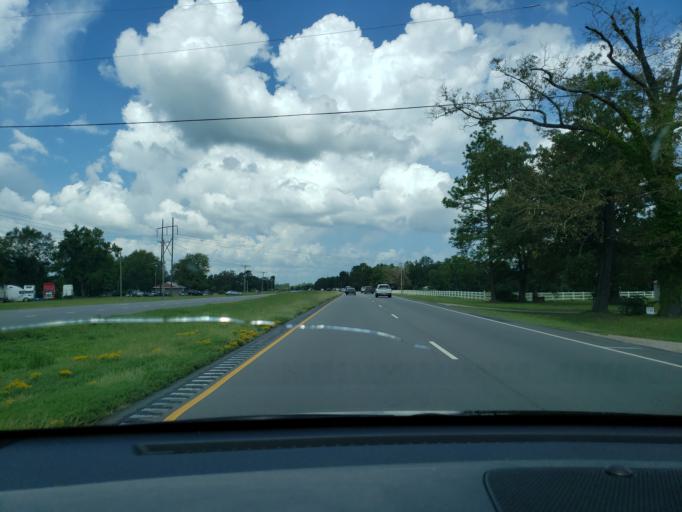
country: US
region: North Carolina
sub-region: Robeson County
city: Saint Pauls
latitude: 34.7728
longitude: -78.8102
